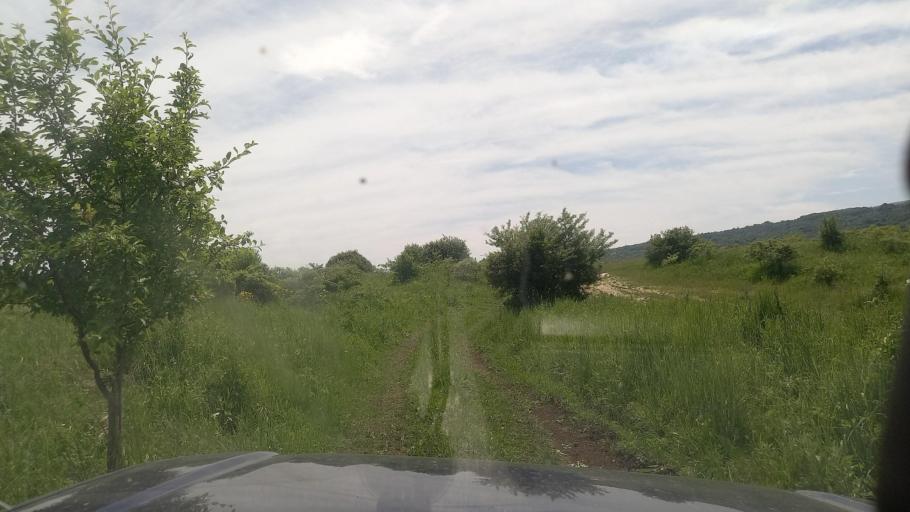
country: RU
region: Karachayevo-Cherkesiya
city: Pregradnaya
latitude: 44.0922
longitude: 41.1450
